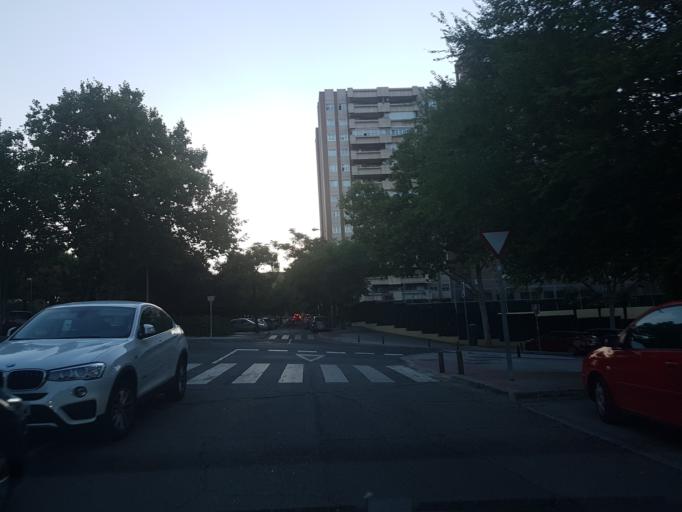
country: ES
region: Madrid
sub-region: Provincia de Madrid
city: Pinar de Chamartin
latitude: 40.4754
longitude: -3.6652
